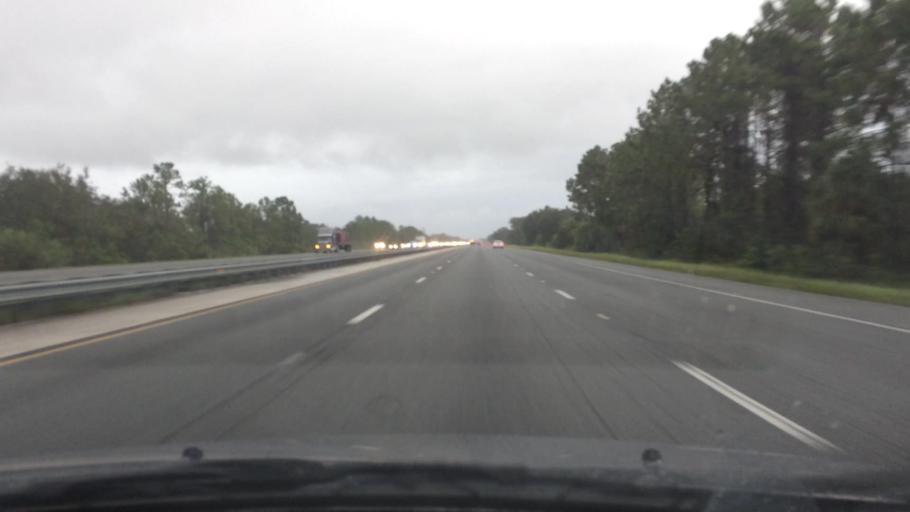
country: US
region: Florida
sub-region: Volusia County
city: Ormond-by-the-Sea
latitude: 29.3083
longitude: -81.1316
